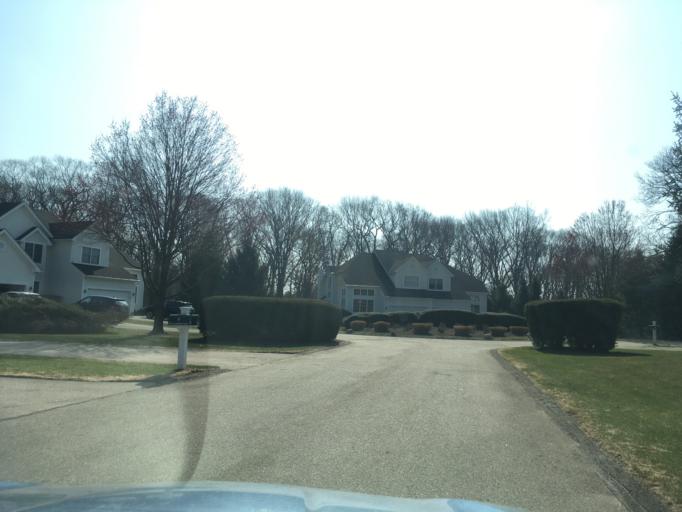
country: US
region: Rhode Island
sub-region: Kent County
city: East Greenwich
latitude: 41.6591
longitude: -71.4821
